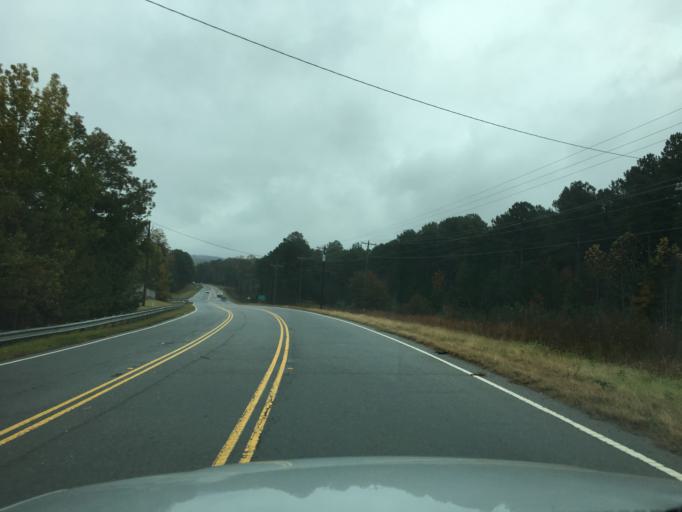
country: US
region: South Carolina
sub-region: Oconee County
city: Utica
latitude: 34.7871
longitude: -82.8938
